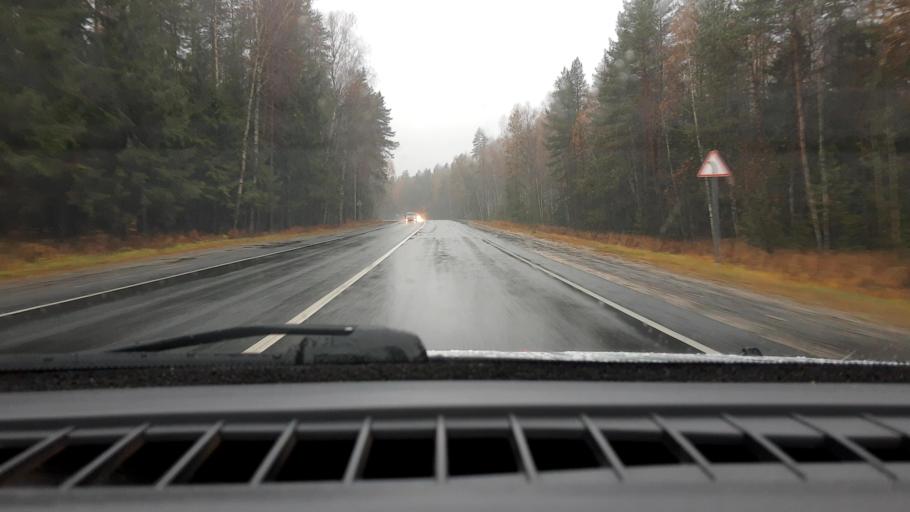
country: RU
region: Nizjnij Novgorod
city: Linda
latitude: 56.6809
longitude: 44.1549
